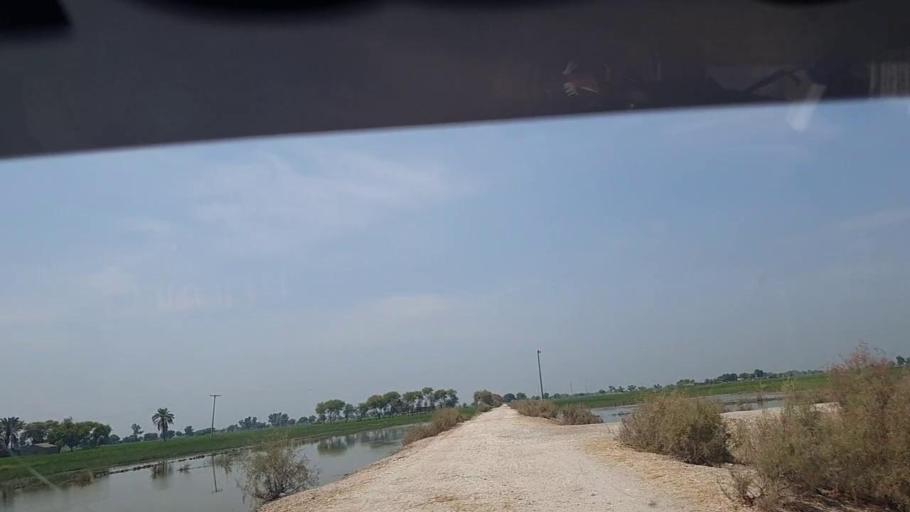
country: PK
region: Sindh
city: Thul
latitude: 28.1710
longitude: 68.7536
